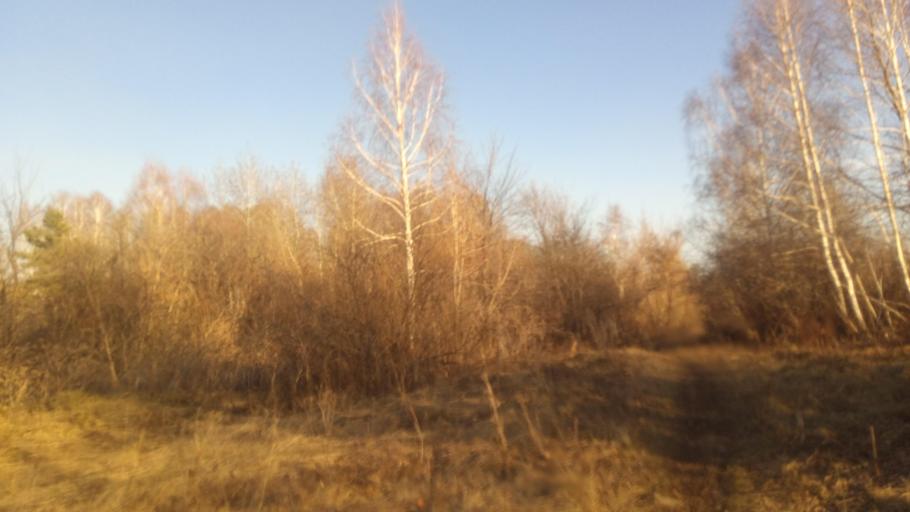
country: RU
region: Chelyabinsk
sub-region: Gorod Chelyabinsk
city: Chelyabinsk
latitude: 55.1514
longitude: 61.3234
